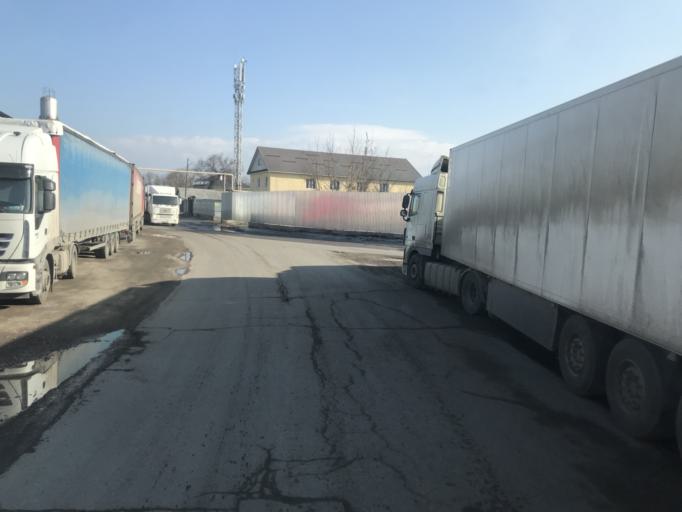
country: KZ
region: Almaty Oblysy
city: Pervomayskiy
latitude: 43.3629
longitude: 76.9791
